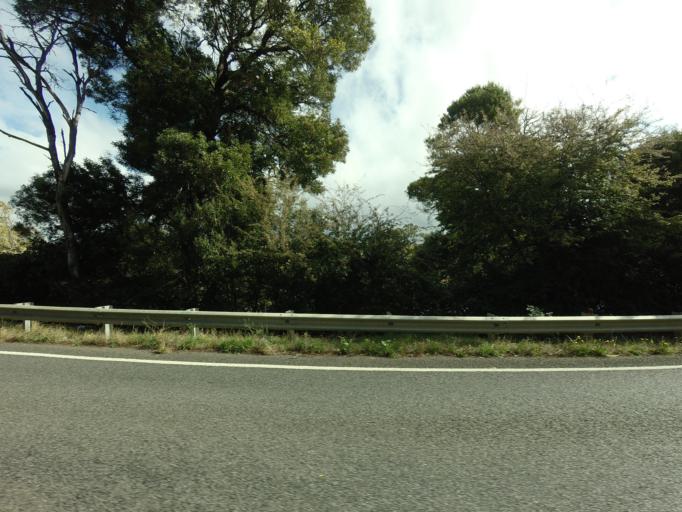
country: AU
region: Tasmania
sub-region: Derwent Valley
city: New Norfolk
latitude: -42.7276
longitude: 146.9557
